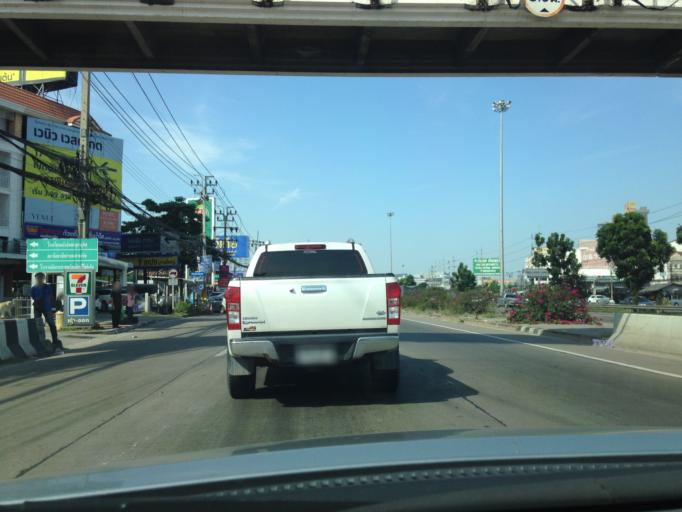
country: TH
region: Nonthaburi
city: Bang Bua Thong
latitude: 13.8680
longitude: 100.4102
